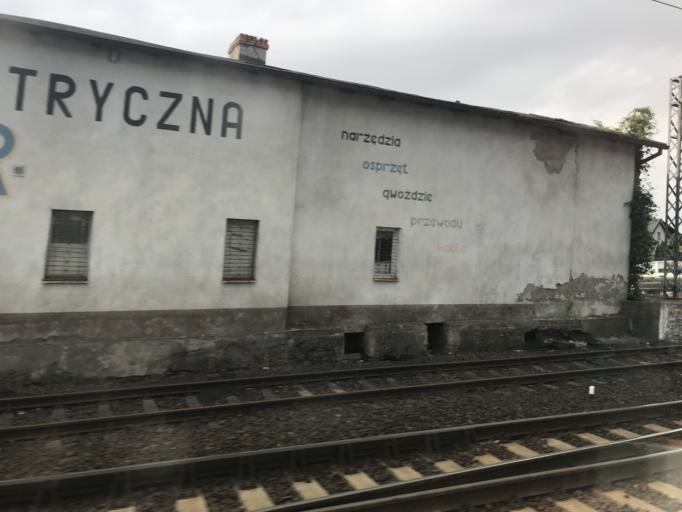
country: PL
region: Pomeranian Voivodeship
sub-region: Powiat tczewski
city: Pelplin
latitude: 53.9258
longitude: 18.7049
